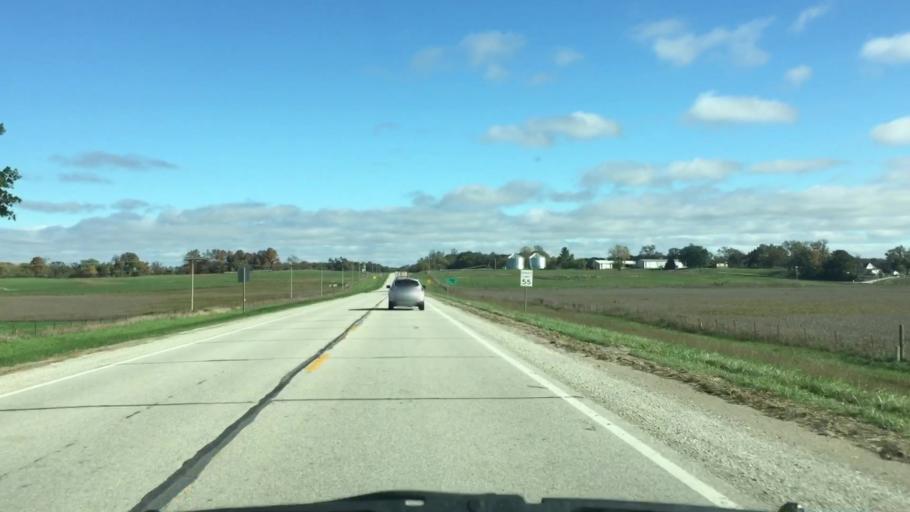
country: US
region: Iowa
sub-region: Decatur County
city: Leon
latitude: 40.6433
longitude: -93.8062
